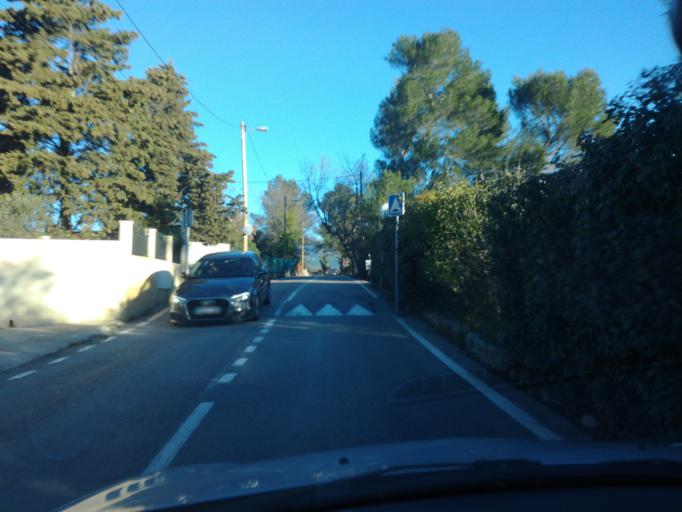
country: FR
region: Provence-Alpes-Cote d'Azur
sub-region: Departement des Alpes-Maritimes
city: La Roquette-sur-Siagne
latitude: 43.6092
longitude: 6.9669
